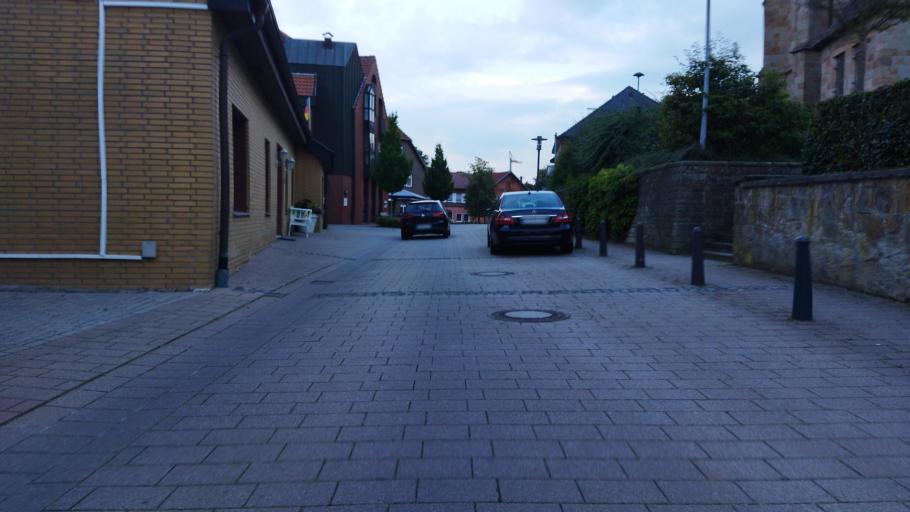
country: DE
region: Lower Saxony
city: Bad Iburg
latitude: 52.1472
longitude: 8.0538
